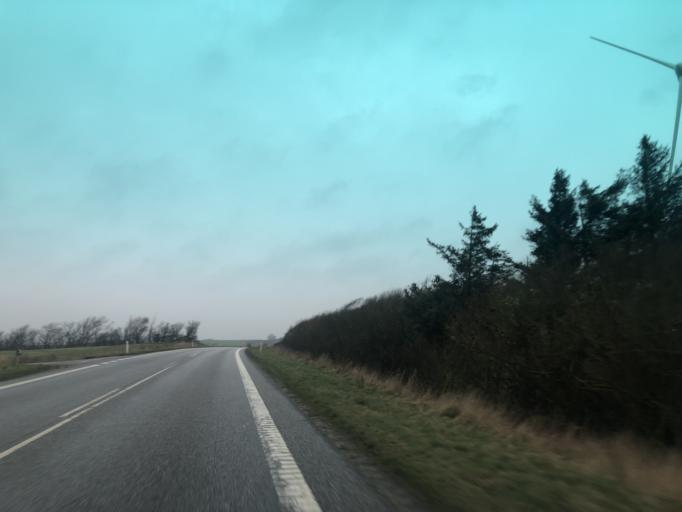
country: DK
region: Central Jutland
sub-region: Struer Kommune
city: Struer
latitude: 56.6271
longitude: 8.5149
